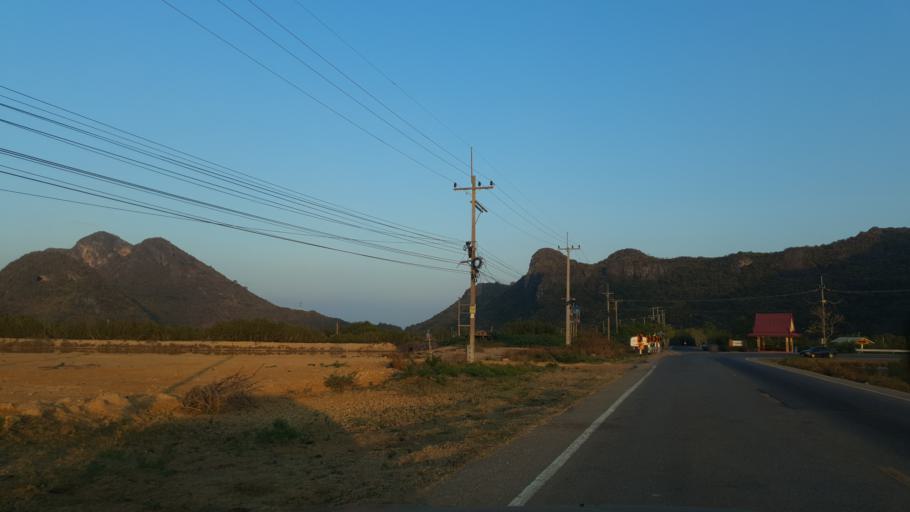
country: TH
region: Prachuap Khiri Khan
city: Sam Roi Yot
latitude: 12.1689
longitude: 99.9904
